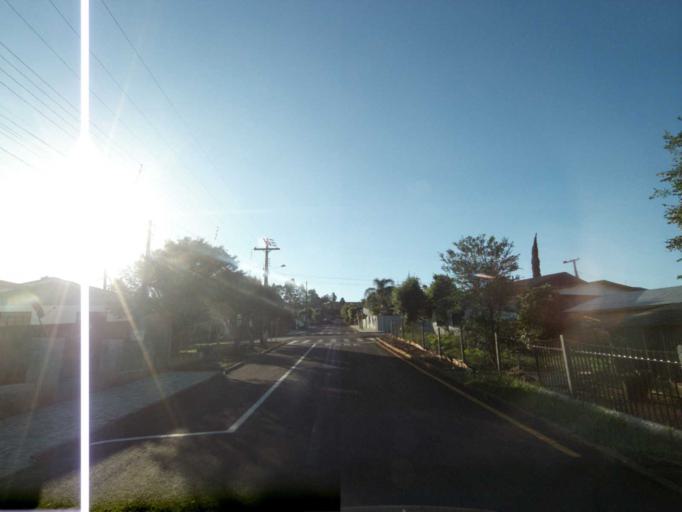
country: BR
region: Parana
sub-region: Coronel Vivida
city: Coronel Vivida
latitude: -25.9746
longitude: -52.8157
